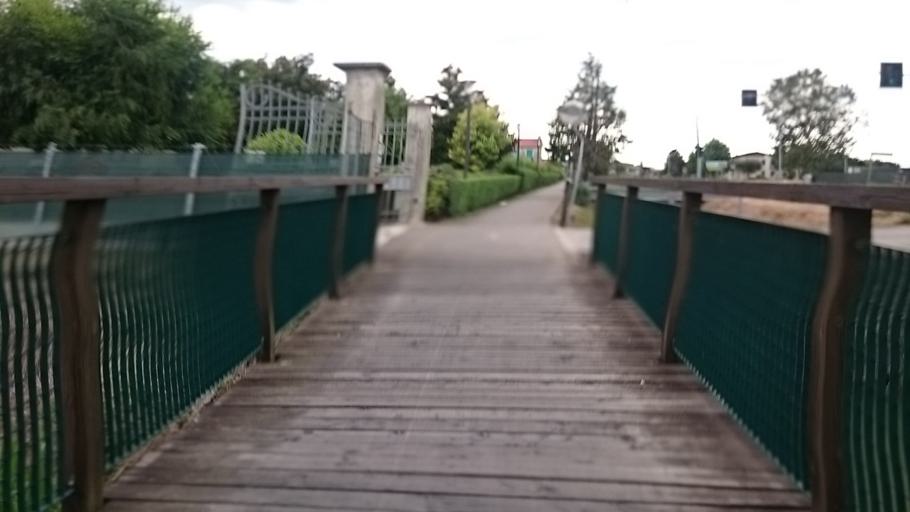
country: IT
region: Veneto
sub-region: Provincia di Padova
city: Masera di Padova
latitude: 45.3175
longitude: 11.8753
